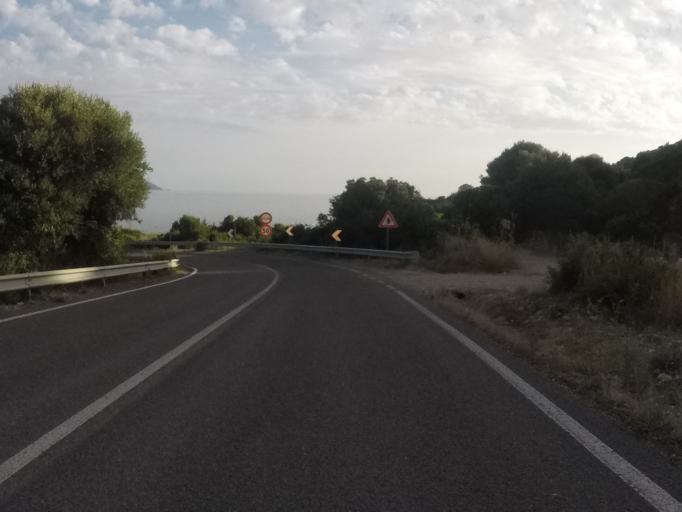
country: IT
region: Sardinia
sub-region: Provincia di Sassari
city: Alghero
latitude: 40.4983
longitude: 8.3680
